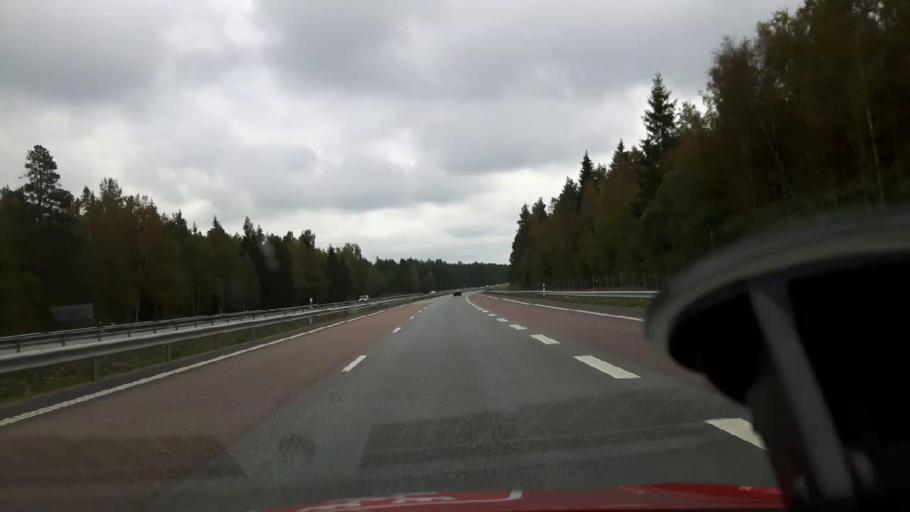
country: SE
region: Gaevleborg
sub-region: Gavle Kommun
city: Gavle
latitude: 60.6365
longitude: 17.1433
